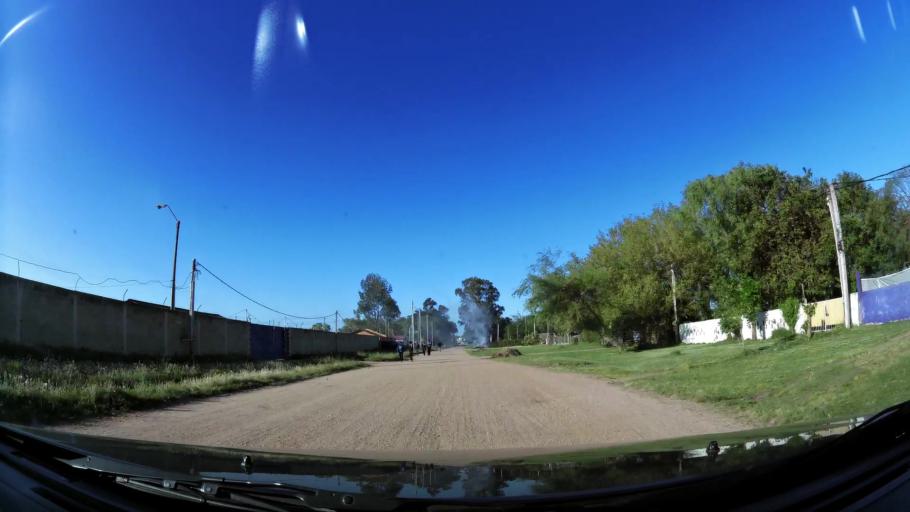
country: UY
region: Canelones
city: Paso de Carrasco
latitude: -34.8564
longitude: -56.0542
